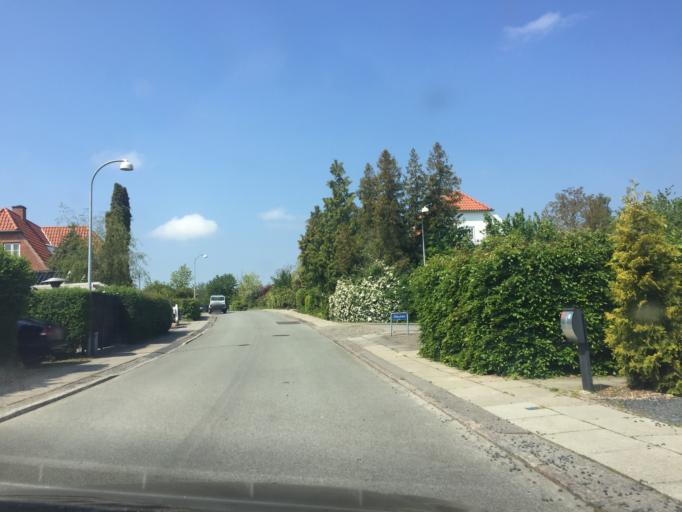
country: DK
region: Capital Region
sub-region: Herlev Kommune
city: Herlev
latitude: 55.7660
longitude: 12.4429
